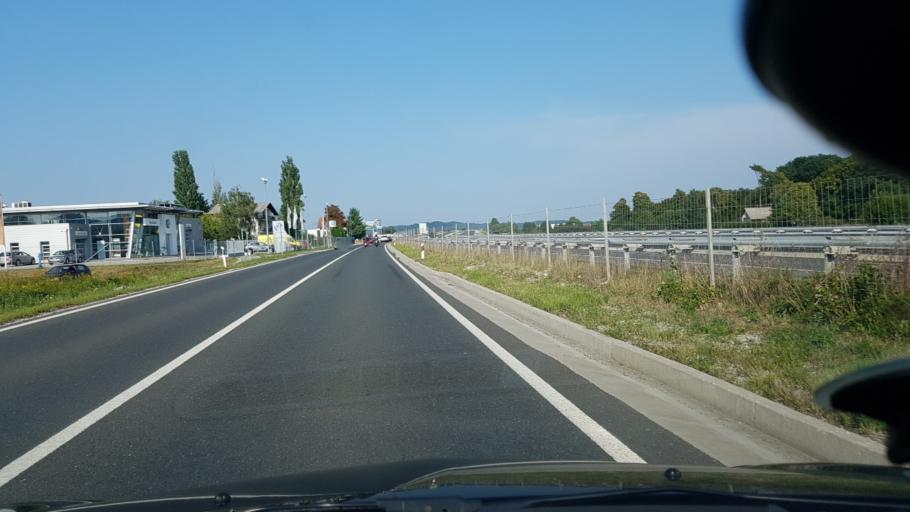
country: HR
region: Krapinsko-Zagorska
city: Oroslavje
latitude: 46.0043
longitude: 15.8698
